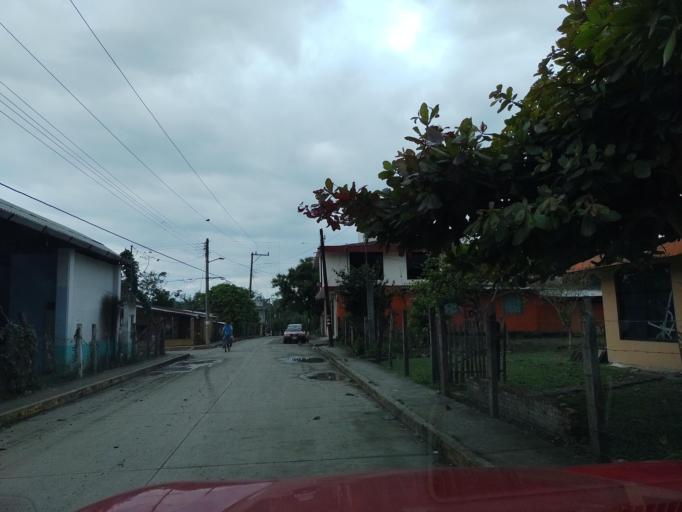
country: MX
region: Veracruz
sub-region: Papantla
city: El Chote
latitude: 20.4303
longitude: -97.3814
